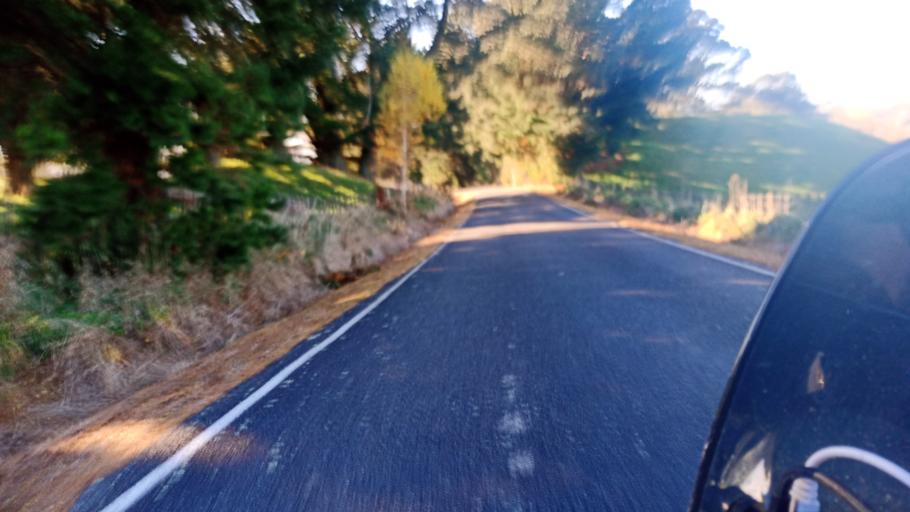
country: NZ
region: Hawke's Bay
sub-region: Wairoa District
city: Wairoa
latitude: -38.8329
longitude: 177.2701
